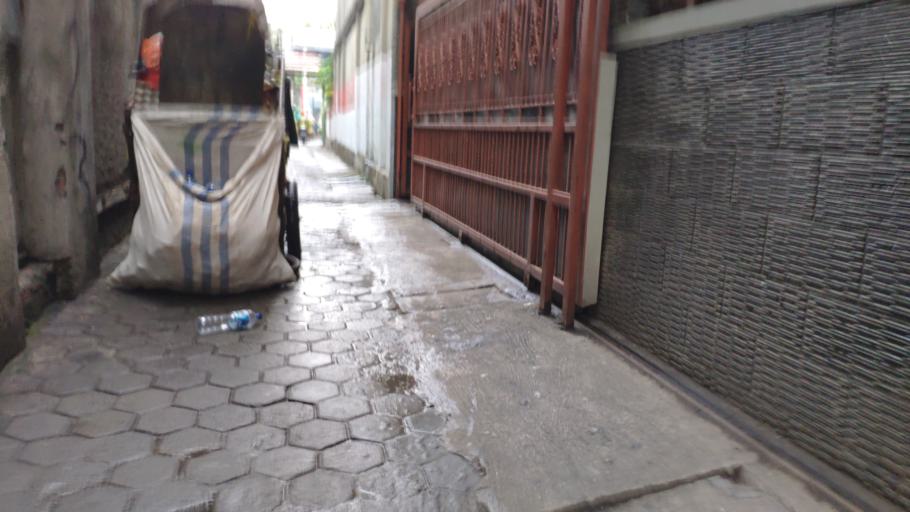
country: ID
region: Jakarta Raya
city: Jakarta
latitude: -6.2042
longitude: 106.8703
